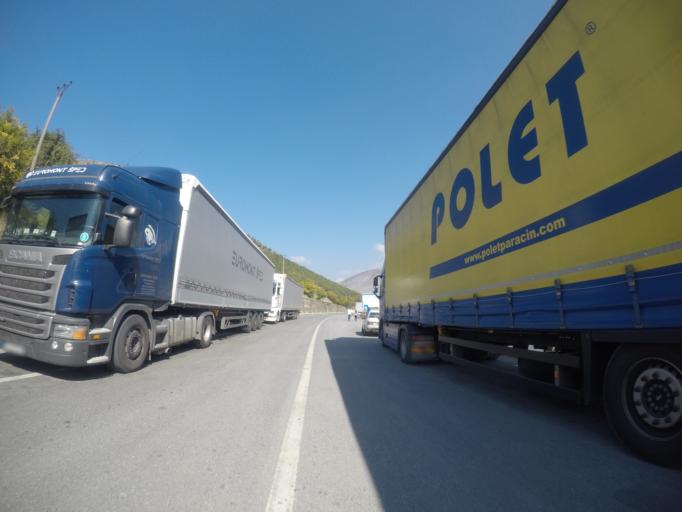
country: AL
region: Shkoder
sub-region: Rrethi i Malesia e Madhe
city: Hot
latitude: 42.3319
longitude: 19.4228
